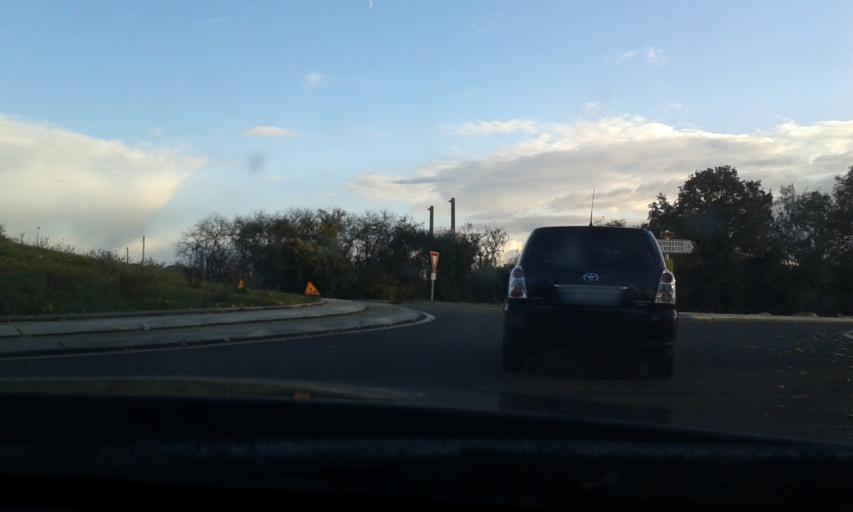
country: FR
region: Centre
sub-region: Departement d'Eure-et-Loir
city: Sours
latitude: 48.3923
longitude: 1.5669
